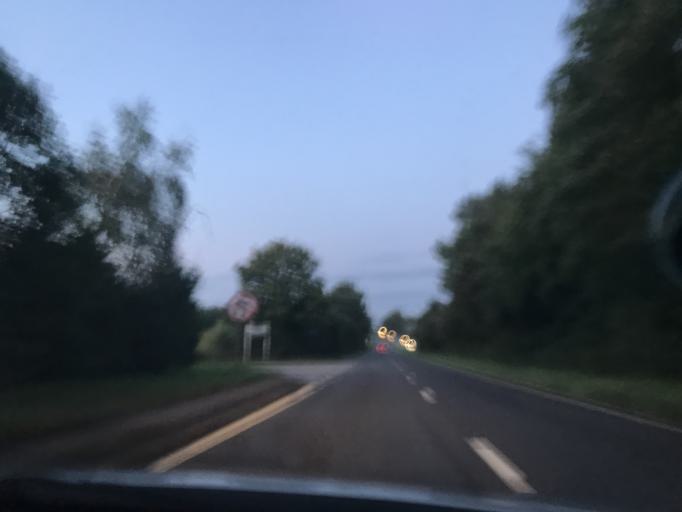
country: GB
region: England
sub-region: Cheshire West and Chester
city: Cuddington
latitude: 53.2354
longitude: -2.5788
